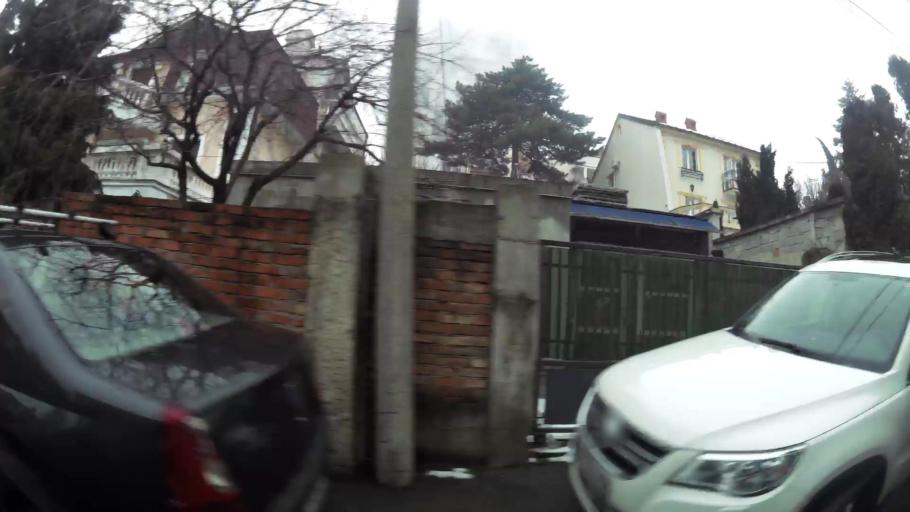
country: RS
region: Central Serbia
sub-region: Belgrade
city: Vozdovac
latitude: 44.7777
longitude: 20.4767
